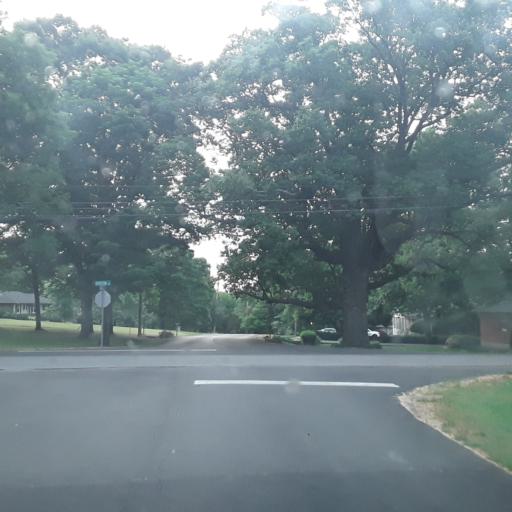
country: US
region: Tennessee
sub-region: Davidson County
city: Oak Hill
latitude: 36.0620
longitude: -86.7624
